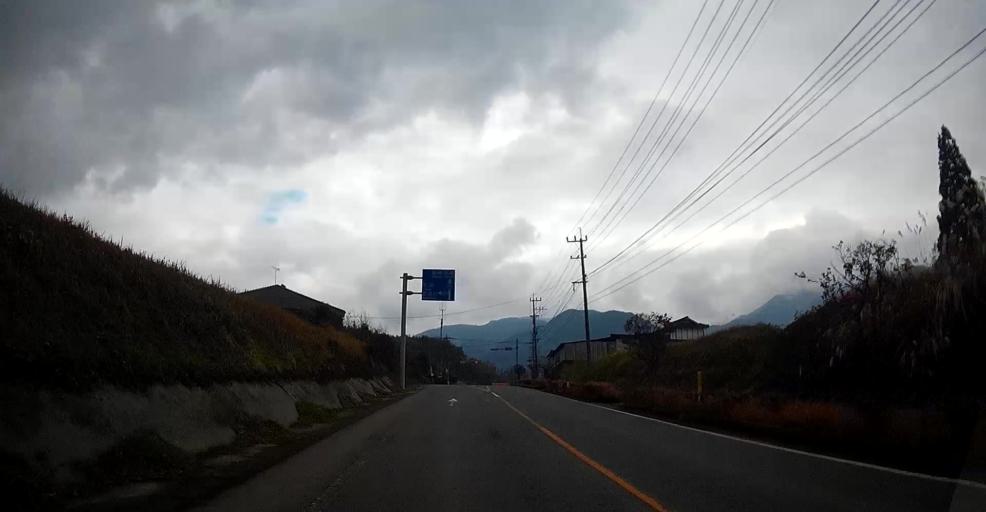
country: JP
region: Kumamoto
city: Matsubase
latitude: 32.6205
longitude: 130.8337
